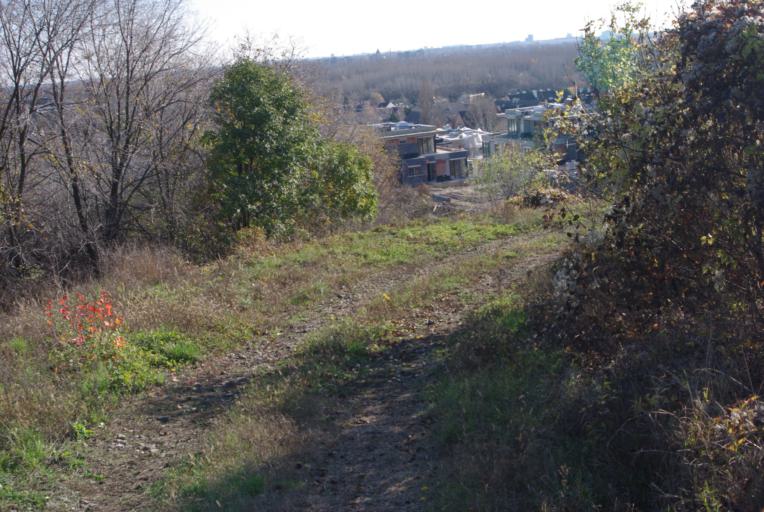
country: HU
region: Pest
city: Urom
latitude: 47.5845
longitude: 19.0379
